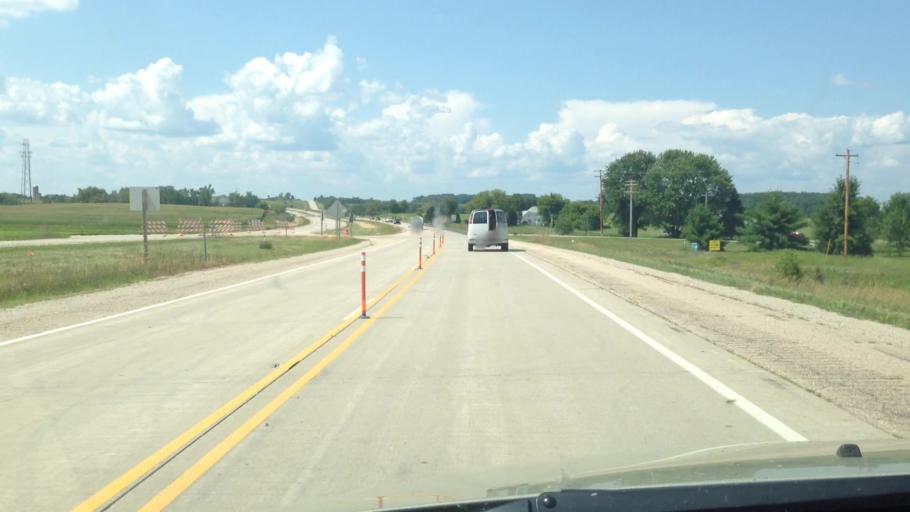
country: US
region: Wisconsin
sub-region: Shawano County
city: Bonduel
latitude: 44.7107
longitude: -88.3823
